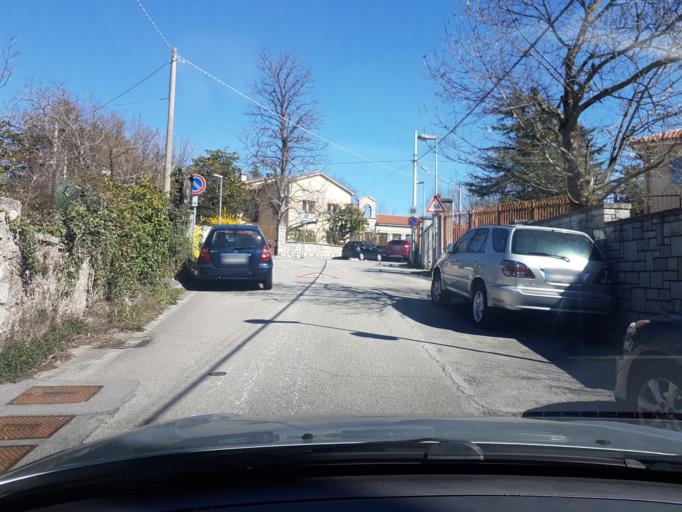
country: IT
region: Friuli Venezia Giulia
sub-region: Provincia di Trieste
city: Sistiana-Visogliano
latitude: 45.7728
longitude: 13.6391
